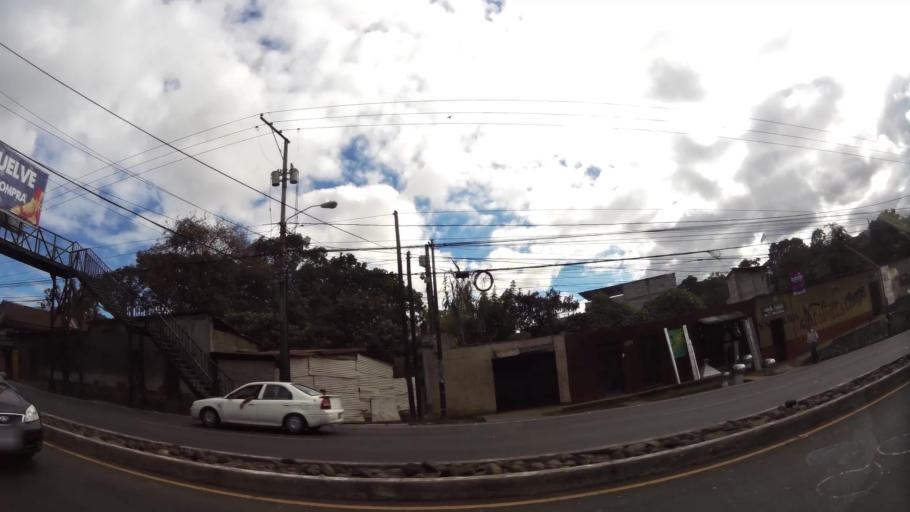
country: GT
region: Guatemala
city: Mixco
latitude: 14.6268
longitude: -90.6057
